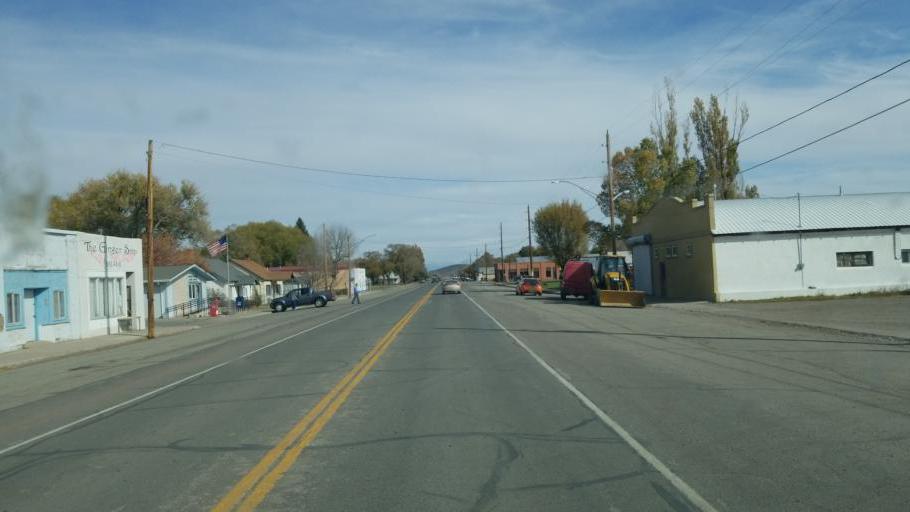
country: US
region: Colorado
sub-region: Conejos County
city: Conejos
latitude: 37.1740
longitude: -105.9370
